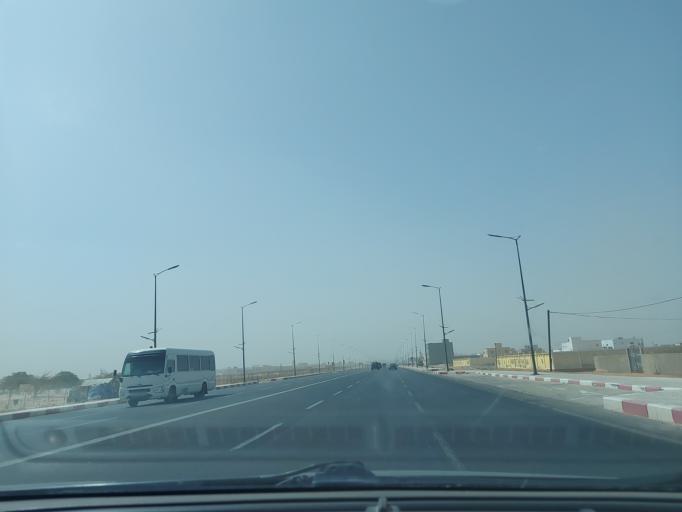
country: MR
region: Nouakchott
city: Nouakchott
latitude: 18.1372
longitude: -16.0053
